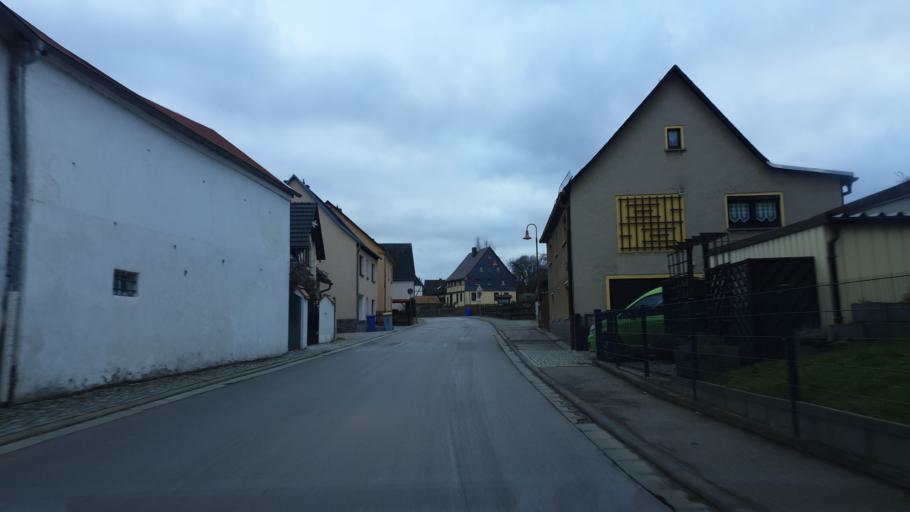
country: DE
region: Saxony
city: Bernsdorf
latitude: 50.7424
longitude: 12.6587
